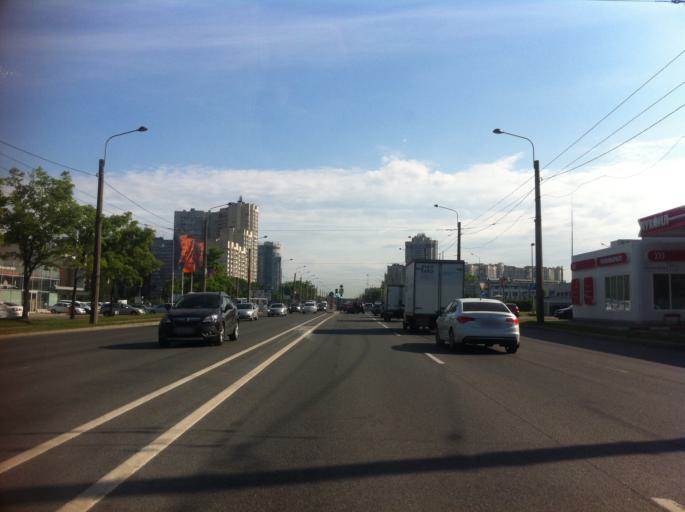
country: RU
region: St.-Petersburg
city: Uritsk
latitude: 59.8475
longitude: 30.2150
